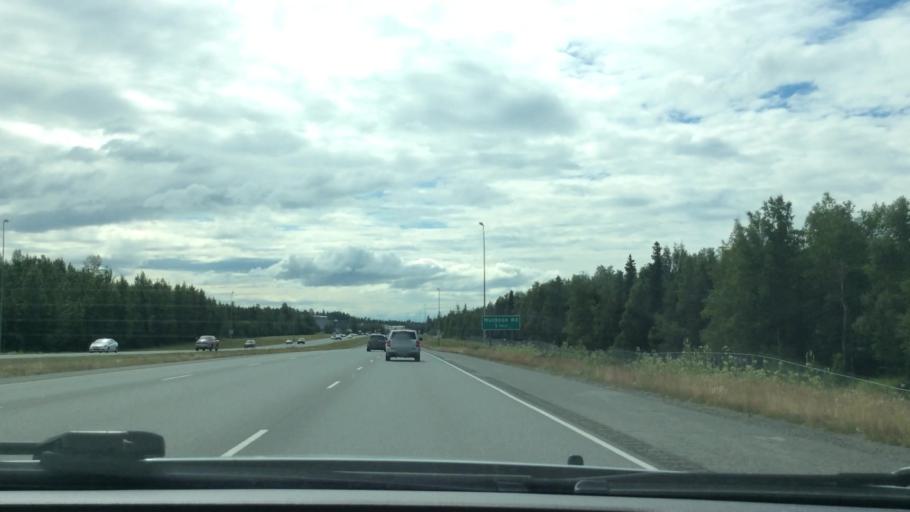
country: US
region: Alaska
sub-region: Anchorage Municipality
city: Elmendorf Air Force Base
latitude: 61.2369
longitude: -149.6984
